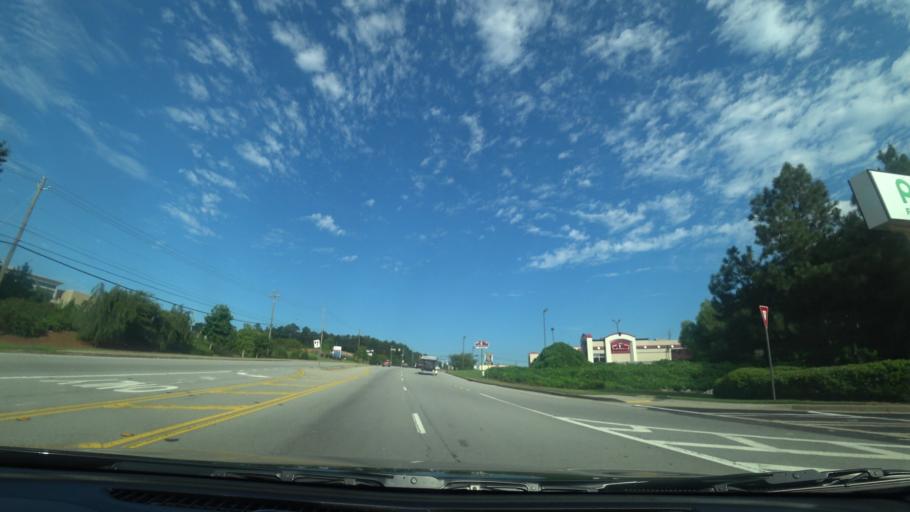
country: US
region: Georgia
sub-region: Rockdale County
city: Conyers
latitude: 33.6826
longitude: -83.9987
